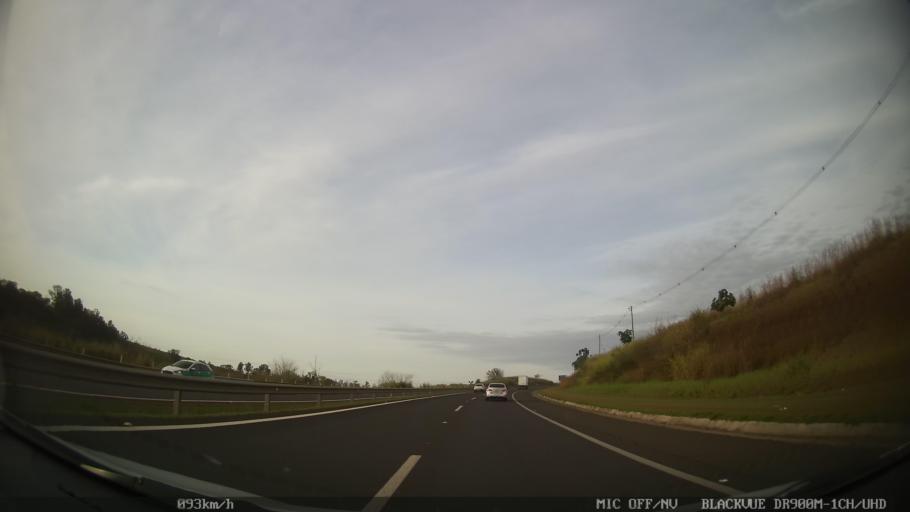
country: BR
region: Sao Paulo
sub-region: Piracicaba
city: Piracicaba
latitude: -22.6827
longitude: -47.5771
